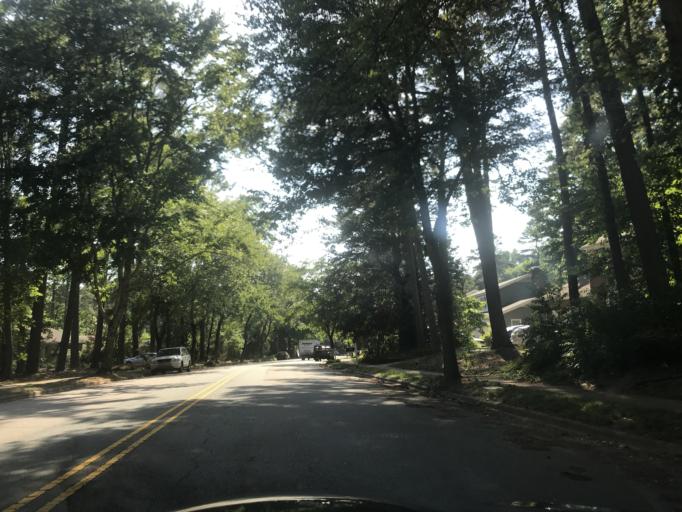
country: US
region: North Carolina
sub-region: Wake County
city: West Raleigh
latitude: 35.8632
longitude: -78.6142
